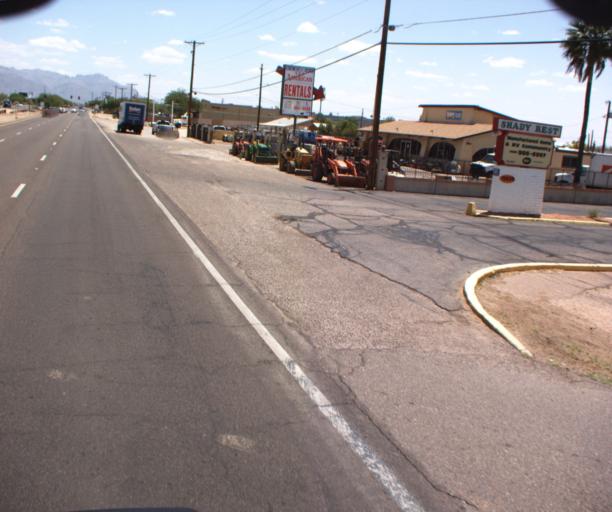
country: US
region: Arizona
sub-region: Pinal County
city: Apache Junction
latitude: 33.4151
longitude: -111.5837
